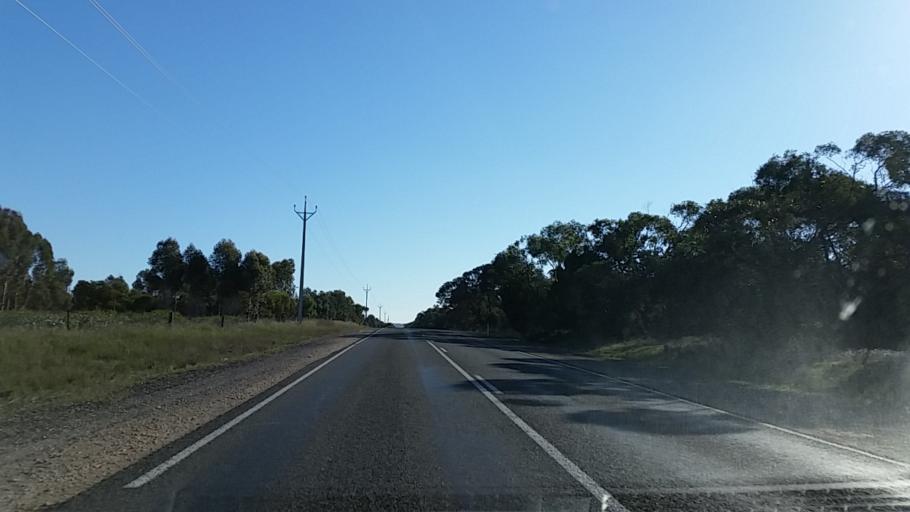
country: AU
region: South Australia
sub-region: Mount Barker
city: Callington
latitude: -35.1187
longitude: 139.1434
